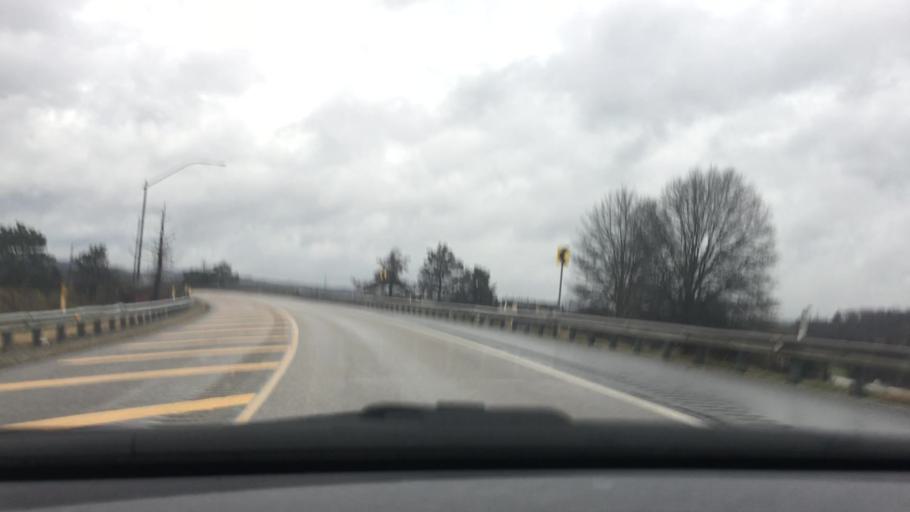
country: US
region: Pennsylvania
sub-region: Butler County
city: Cranberry Township
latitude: 40.6645
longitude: -80.0918
